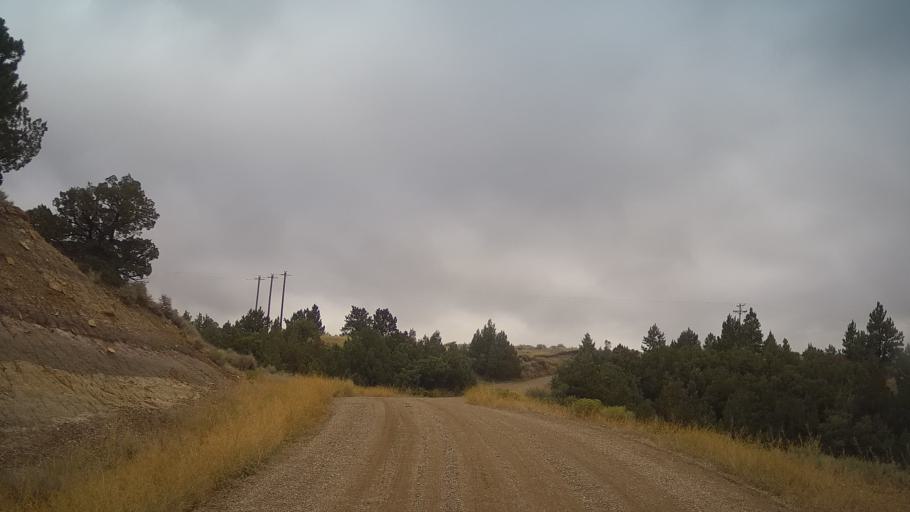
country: US
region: Montana
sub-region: Dawson County
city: Glendive
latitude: 47.0492
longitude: -104.6788
